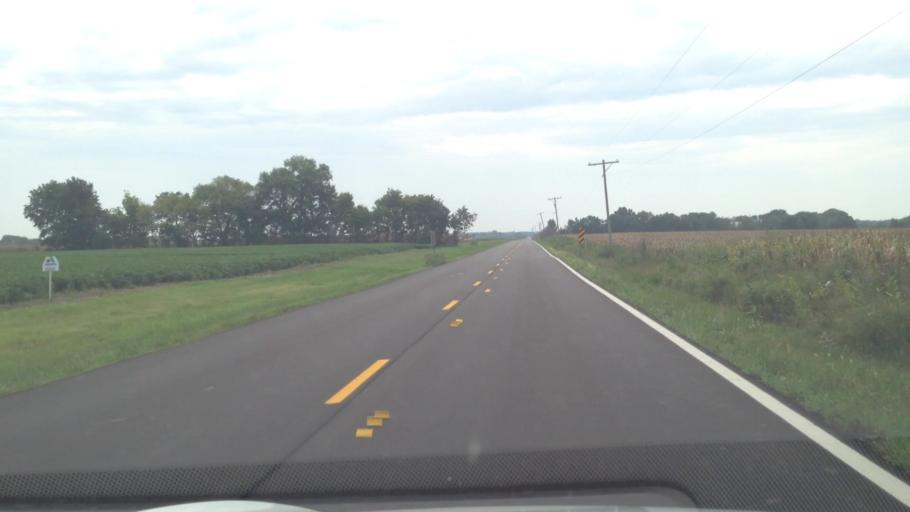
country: US
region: Kansas
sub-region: Crawford County
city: Girard
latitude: 37.6271
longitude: -94.9698
